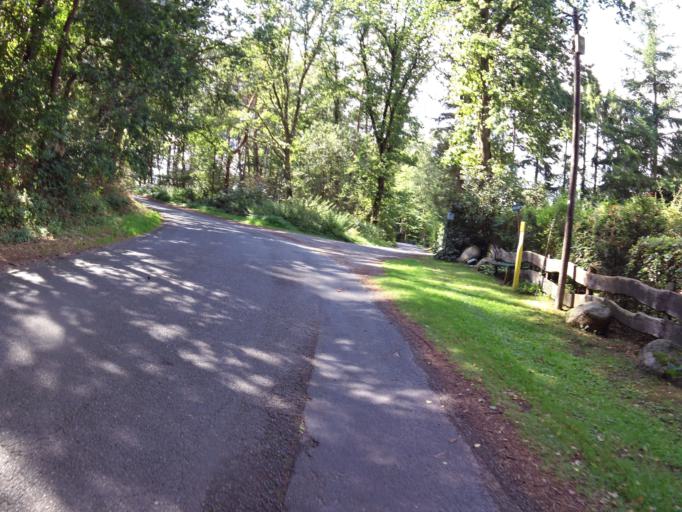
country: DE
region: Lower Saxony
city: Seedorf
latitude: 53.3321
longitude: 9.1973
